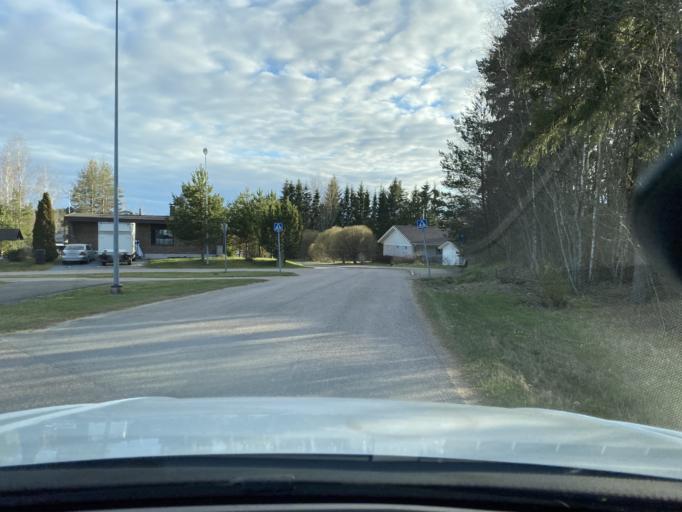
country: FI
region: Pirkanmaa
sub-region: Lounais-Pirkanmaa
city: Punkalaidun
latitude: 61.1146
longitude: 23.1019
